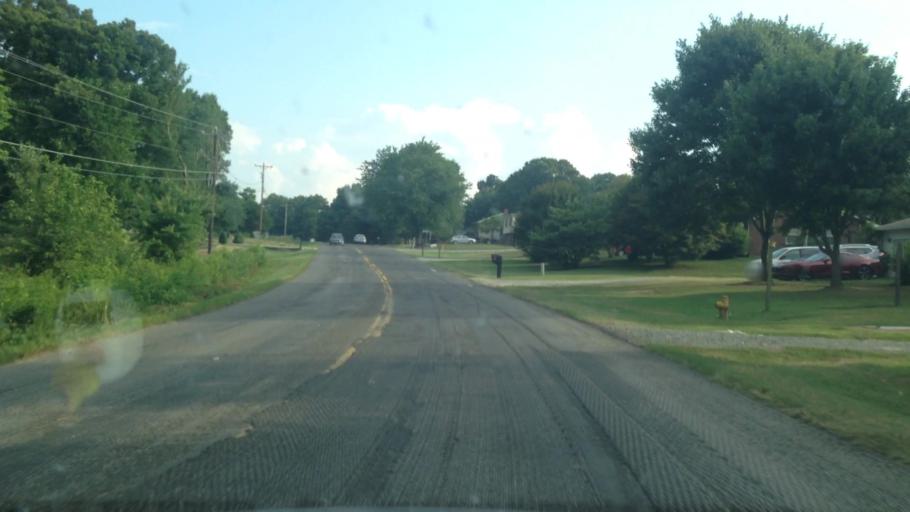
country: US
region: North Carolina
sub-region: Forsyth County
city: Kernersville
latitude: 36.0605
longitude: -80.0653
